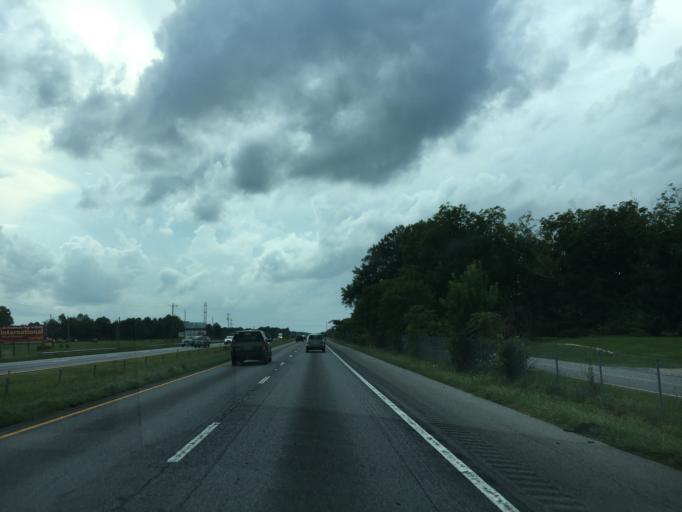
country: US
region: South Carolina
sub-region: Spartanburg County
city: Cowpens
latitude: 35.0750
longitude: -81.7425
